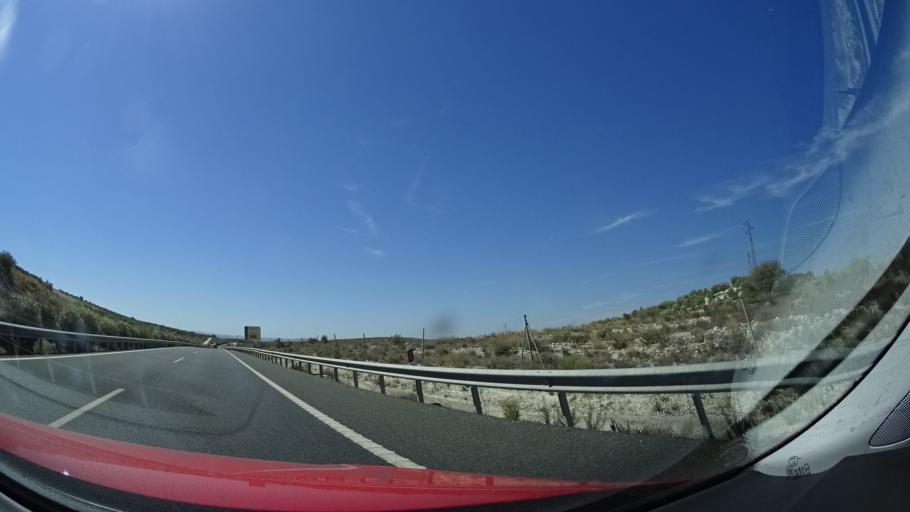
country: ES
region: Andalusia
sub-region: Provincia de Sevilla
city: Gilena
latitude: 37.2832
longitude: -4.9159
